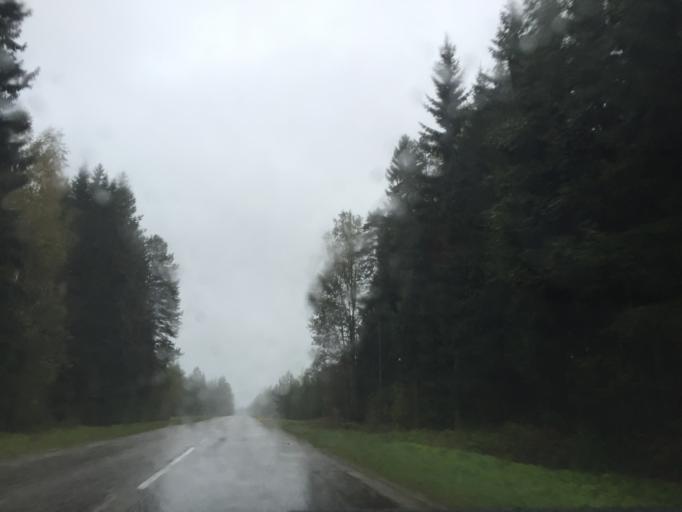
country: LV
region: Ropazu
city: Ropazi
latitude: 57.0095
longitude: 24.6786
